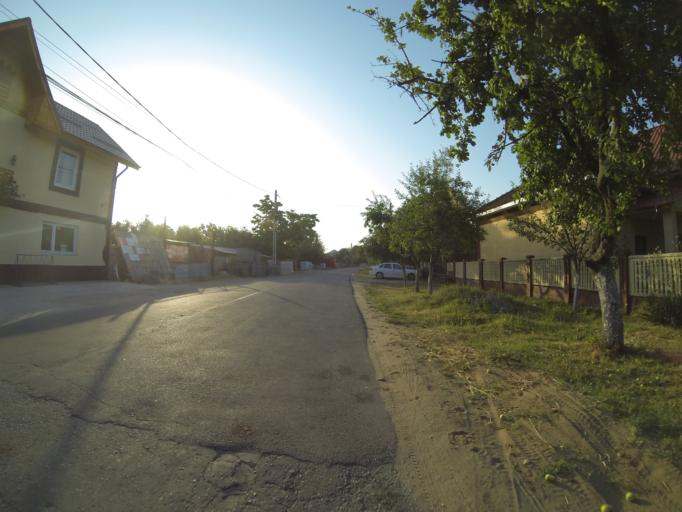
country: RO
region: Dolj
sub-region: Comuna Dobrotesti
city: Dobrotesti
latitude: 43.9596
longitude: 24.1314
